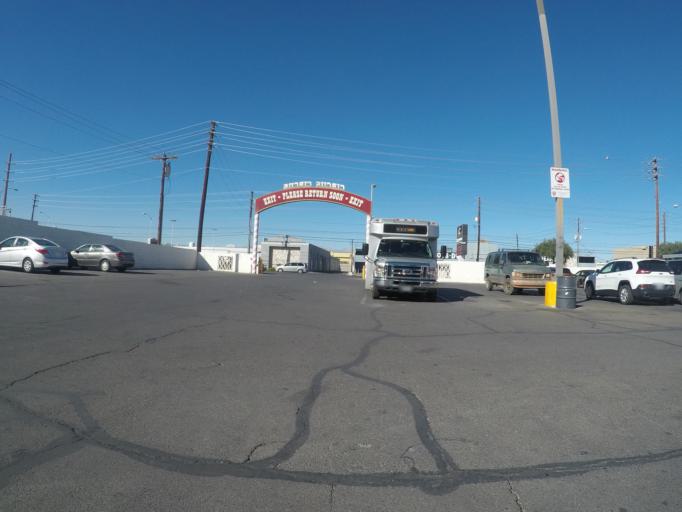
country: US
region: Nevada
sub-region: Clark County
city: Paradise
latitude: 36.1374
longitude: -115.1685
